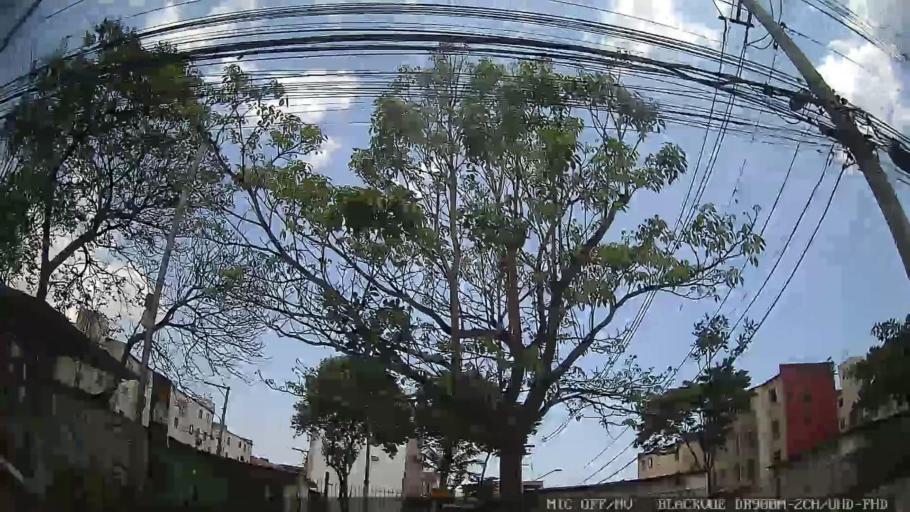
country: BR
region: Sao Paulo
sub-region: Taboao Da Serra
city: Taboao da Serra
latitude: -23.6695
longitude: -46.7854
